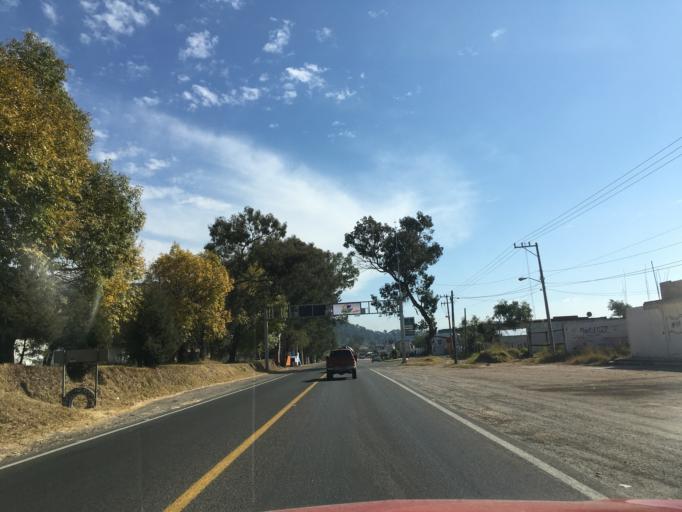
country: MX
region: Michoacan
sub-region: Hidalgo
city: Colonia Ecologica Asociacion de Lucha Social (Lucha Social)
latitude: 19.6987
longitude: -100.5997
